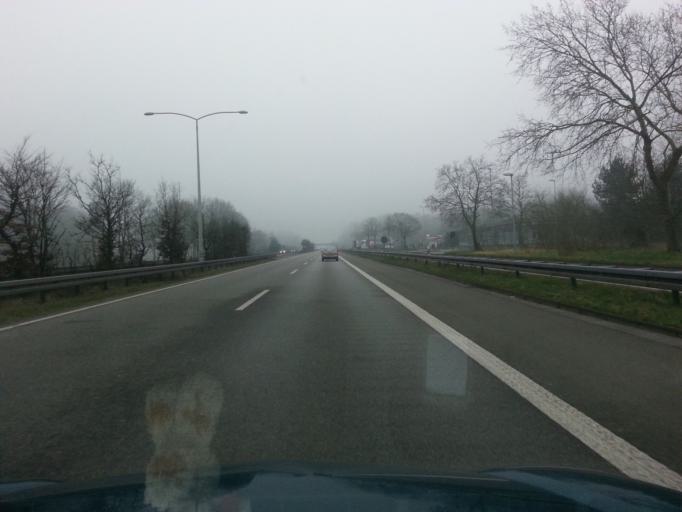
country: NL
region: Gelderland
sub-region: Gemeente Montferland
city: s-Heerenberg
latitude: 51.8989
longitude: 6.1652
